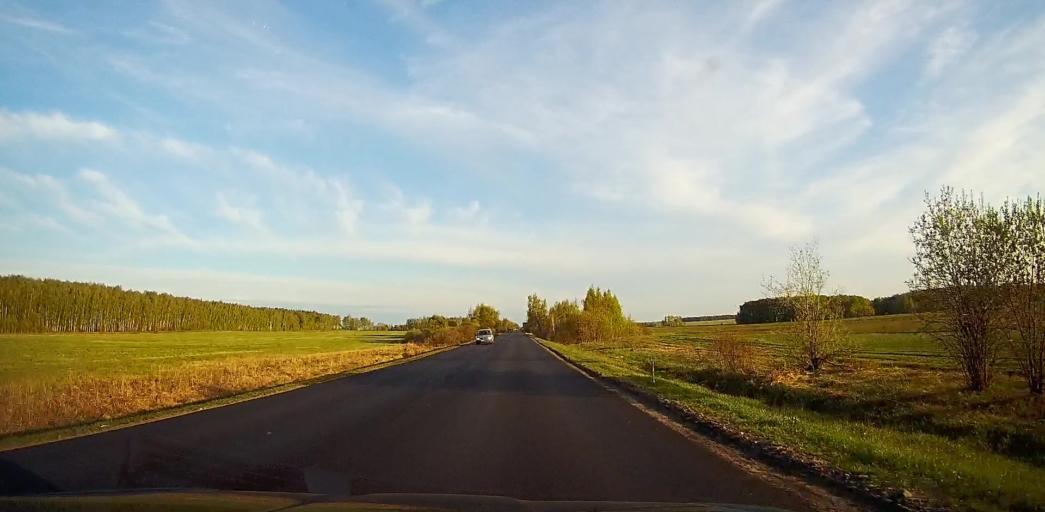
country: RU
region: Moskovskaya
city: Bronnitsy
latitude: 55.2859
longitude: 38.2161
